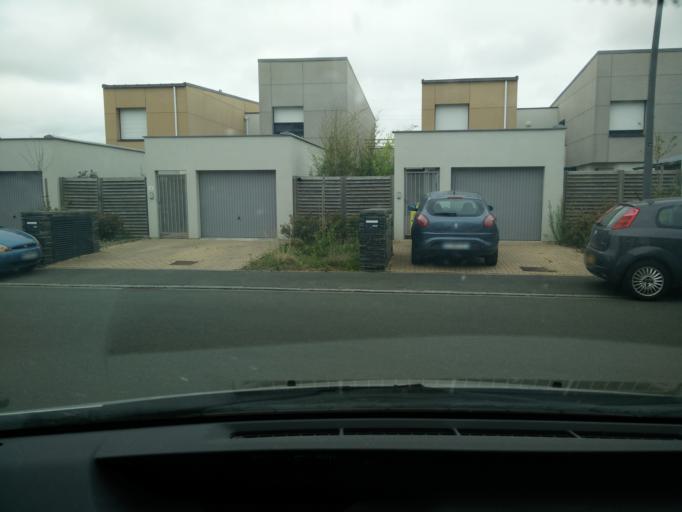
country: FR
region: Pays de la Loire
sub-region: Departement de Maine-et-Loire
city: Angers
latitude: 47.4705
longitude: -0.5090
